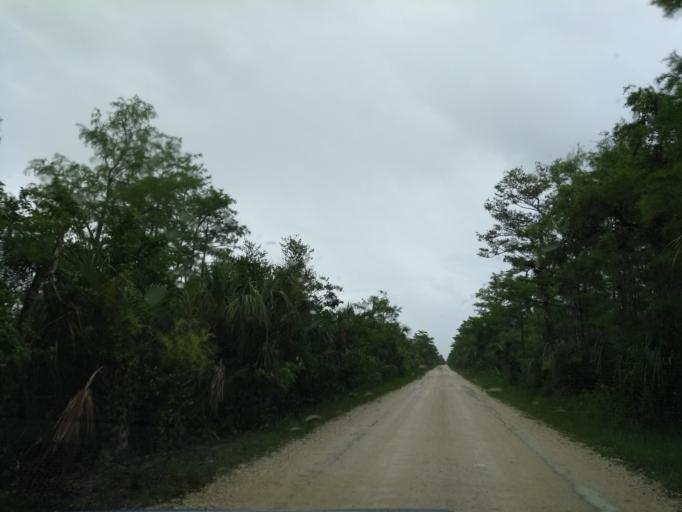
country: US
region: Florida
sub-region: Miami-Dade County
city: The Hammocks
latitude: 25.7602
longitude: -81.0175
